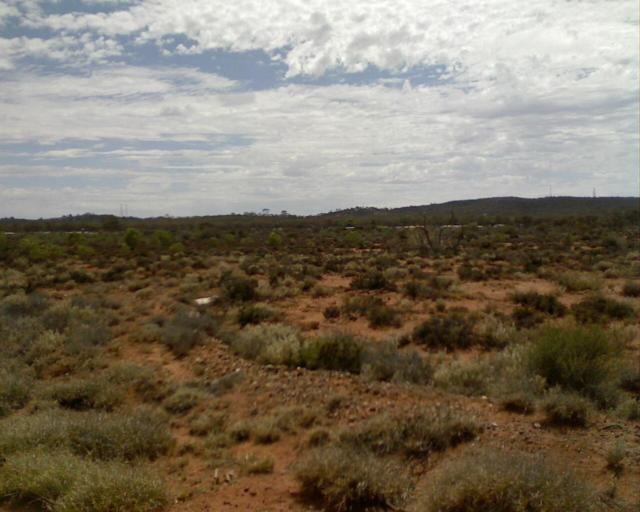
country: AU
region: Western Australia
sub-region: Kalgoorlie/Boulder
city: Stoneville
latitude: -31.2164
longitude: 121.6495
